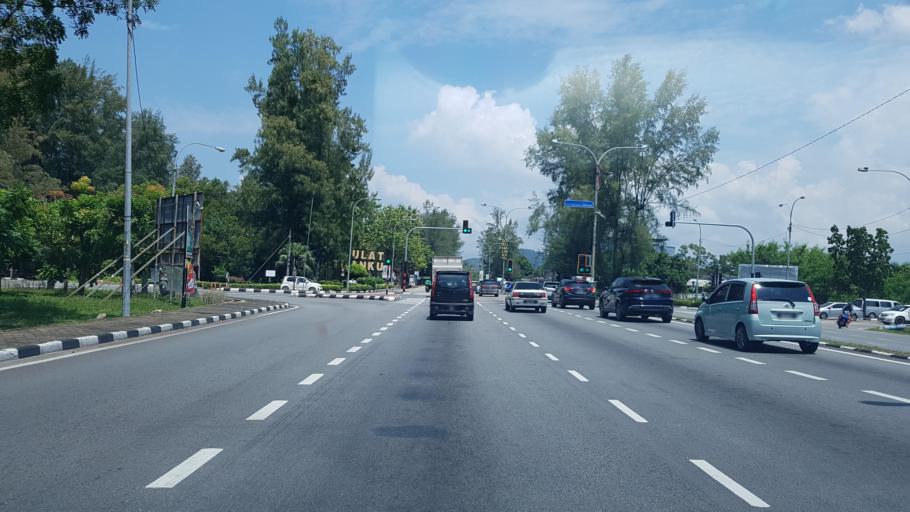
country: MY
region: Terengganu
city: Kuala Terengganu
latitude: 5.2858
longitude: 103.1689
